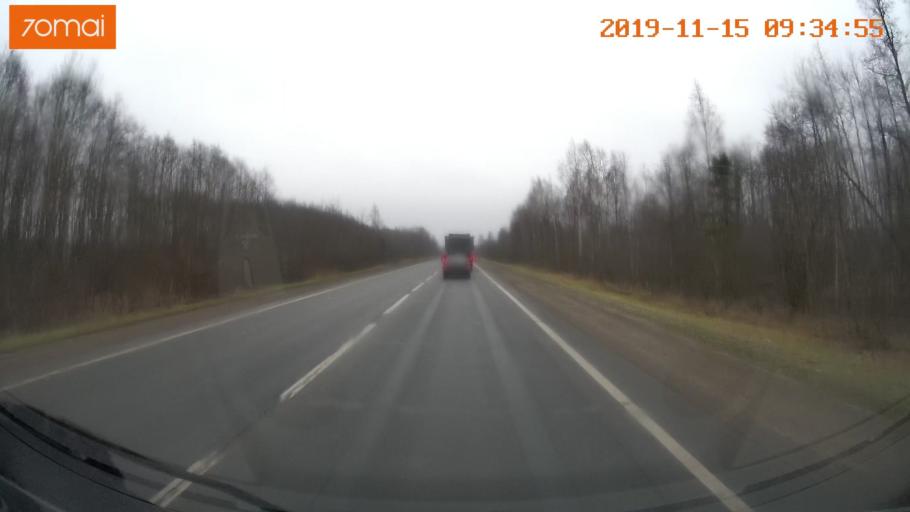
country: RU
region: Vologda
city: Sheksna
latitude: 59.2571
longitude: 38.3894
